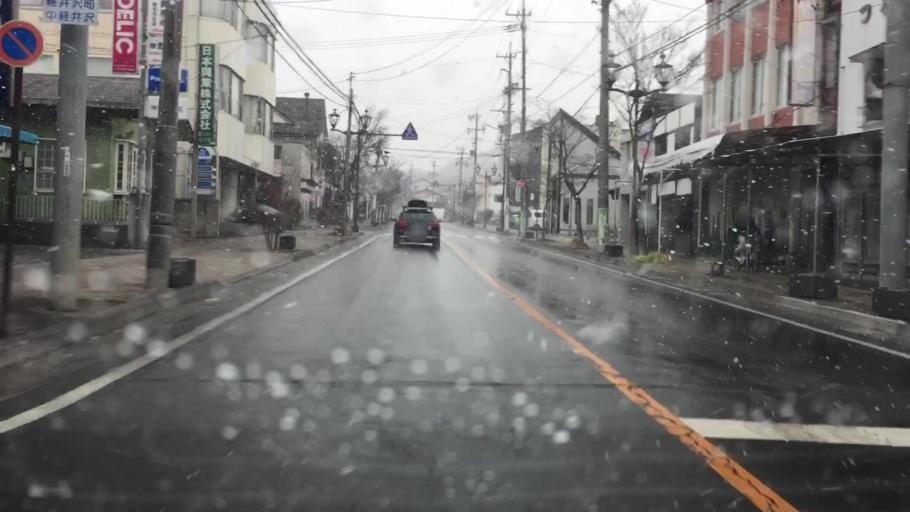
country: JP
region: Nagano
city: Komoro
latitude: 36.3496
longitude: 138.5916
